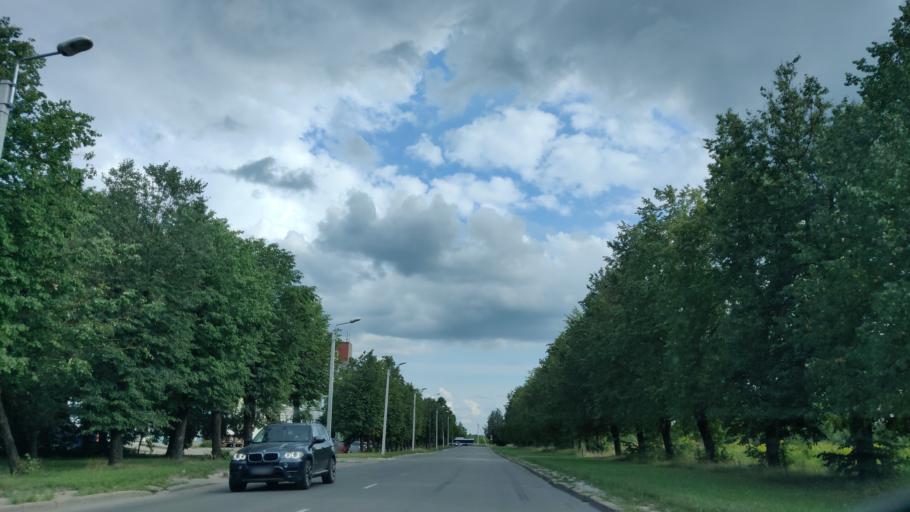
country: LT
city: Baltoji Voke
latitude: 54.6223
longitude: 25.1424
